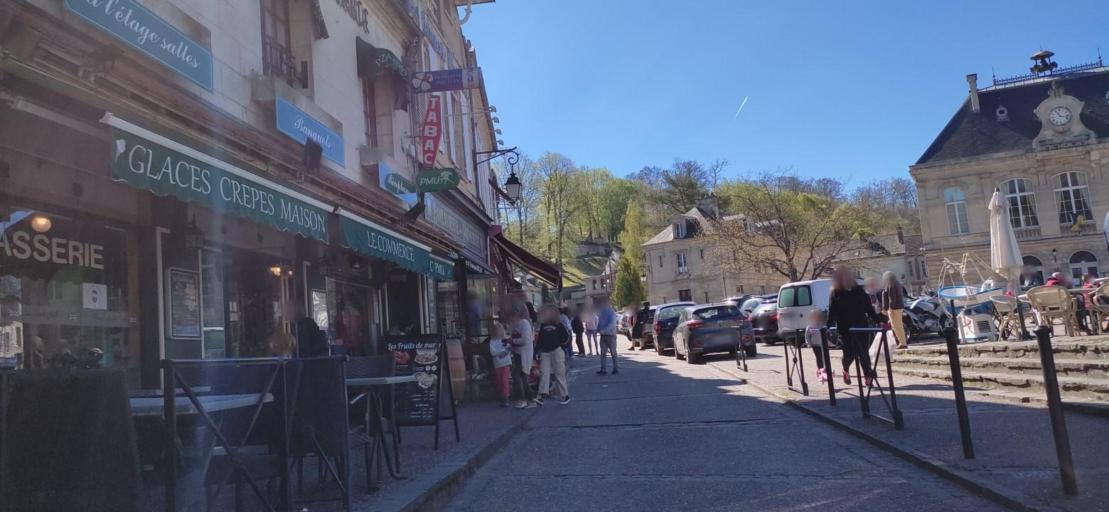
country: FR
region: Picardie
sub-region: Departement de l'Oise
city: Pierrefonds
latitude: 49.3480
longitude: 2.9781
